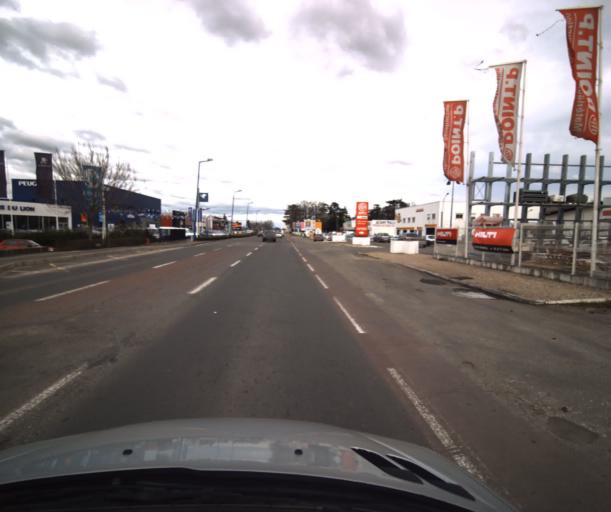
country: FR
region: Midi-Pyrenees
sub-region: Departement du Tarn-et-Garonne
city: Montauban
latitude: 44.0339
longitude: 1.3760
